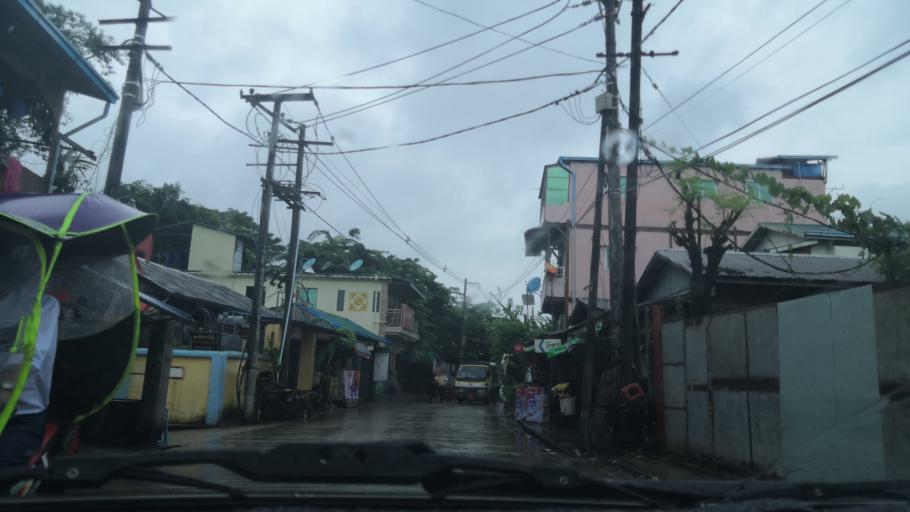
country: MM
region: Yangon
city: Yangon
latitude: 16.8791
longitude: 96.1481
